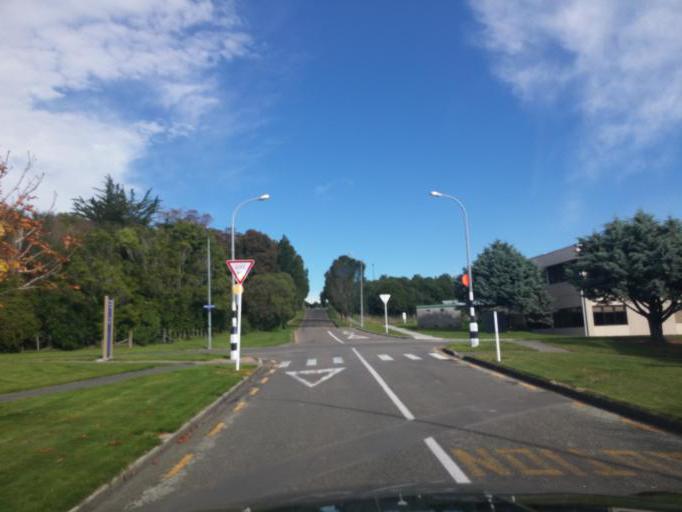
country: NZ
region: Manawatu-Wanganui
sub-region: Palmerston North City
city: Palmerston North
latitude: -40.3899
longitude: 175.6195
